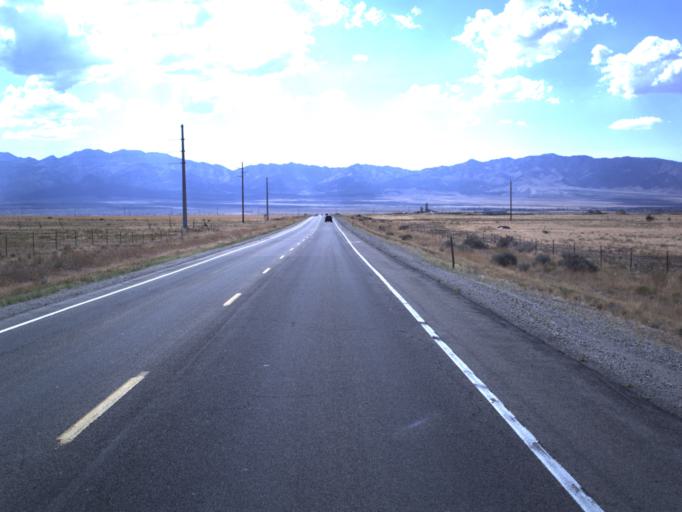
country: US
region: Utah
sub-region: Tooele County
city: Tooele
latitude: 40.5508
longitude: -112.3221
